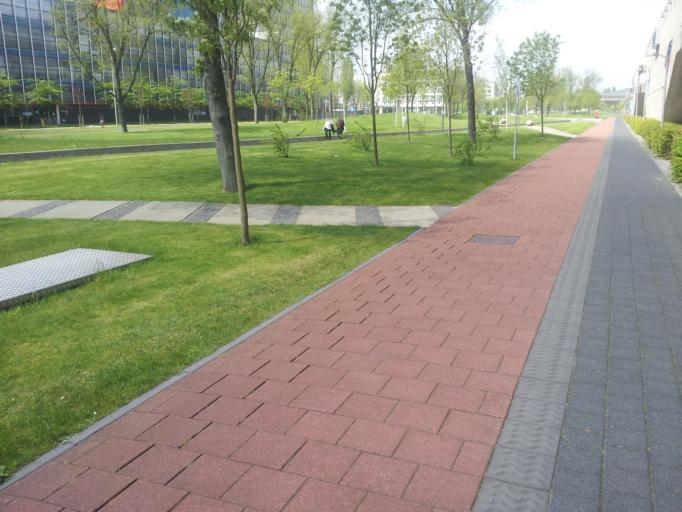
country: NL
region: South Holland
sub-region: Gemeente Delft
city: Delft
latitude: 51.9979
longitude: 4.3751
